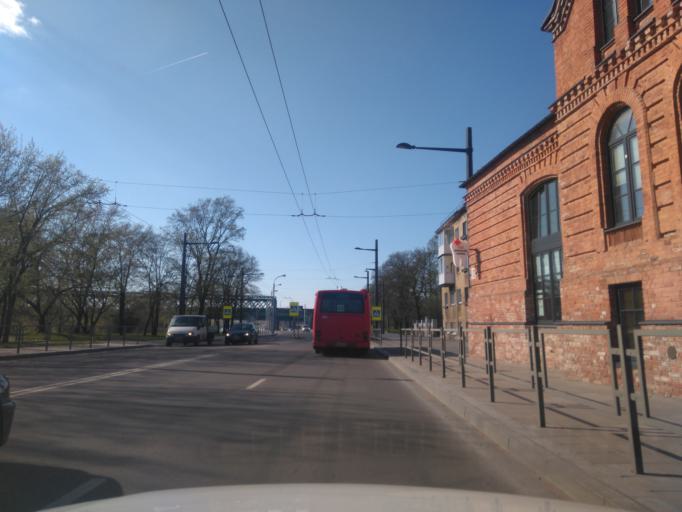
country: LT
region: Kauno apskritis
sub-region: Kaunas
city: Aleksotas
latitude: 54.8810
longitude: 23.9291
